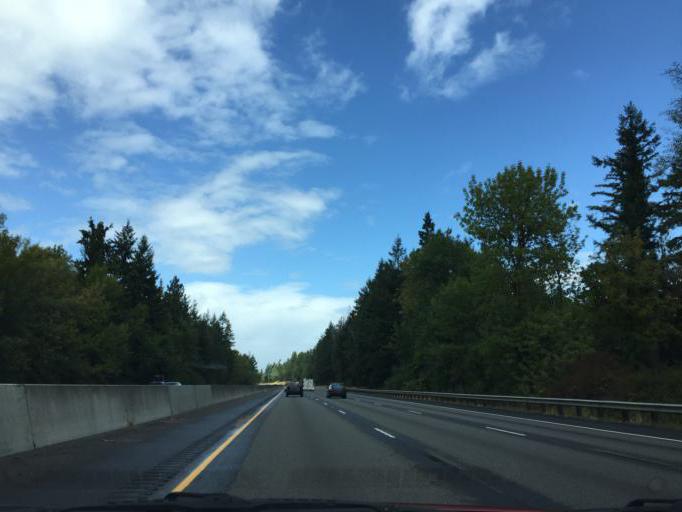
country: US
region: Washington
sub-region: Thurston County
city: Grand Mound
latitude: 46.8546
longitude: -122.9759
